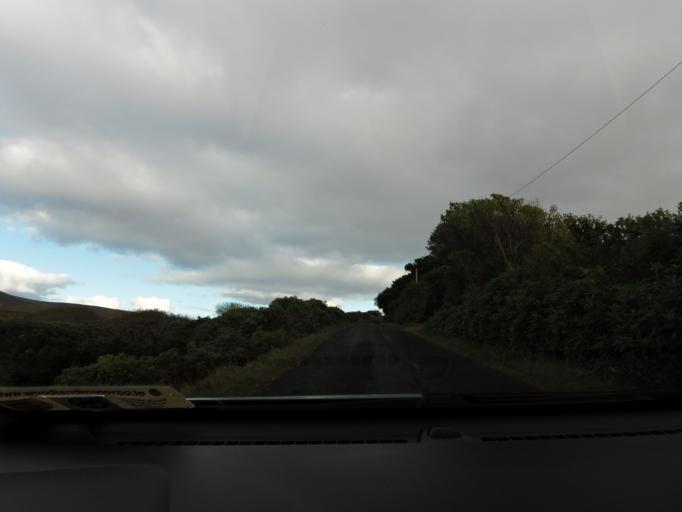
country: IE
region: Connaught
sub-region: Maigh Eo
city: Belmullet
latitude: 53.9281
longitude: -10.0161
